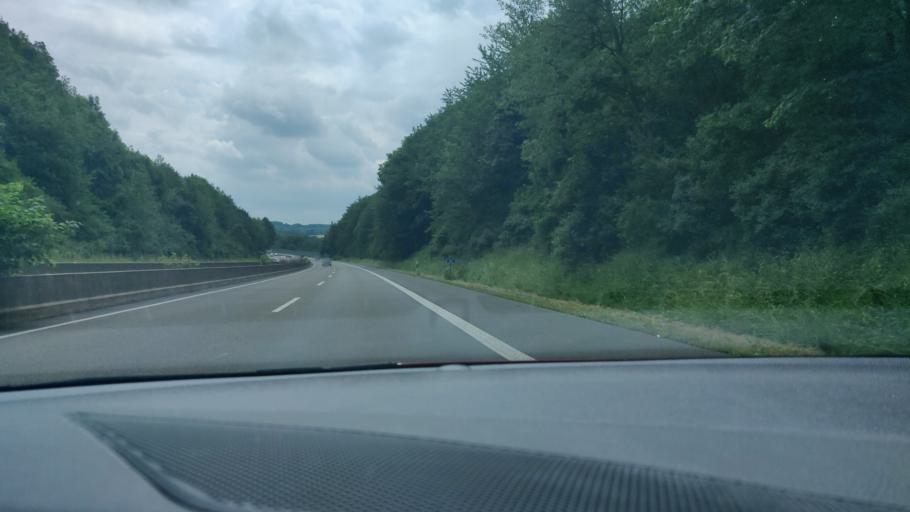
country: DE
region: North Rhine-Westphalia
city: Wulfrath
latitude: 51.2866
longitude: 7.0717
